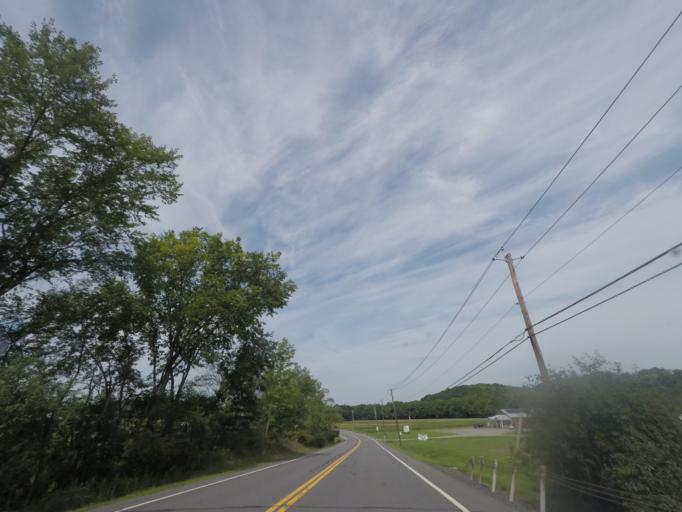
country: US
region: New York
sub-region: Rensselaer County
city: Wynantskill
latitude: 42.7308
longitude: -73.6135
